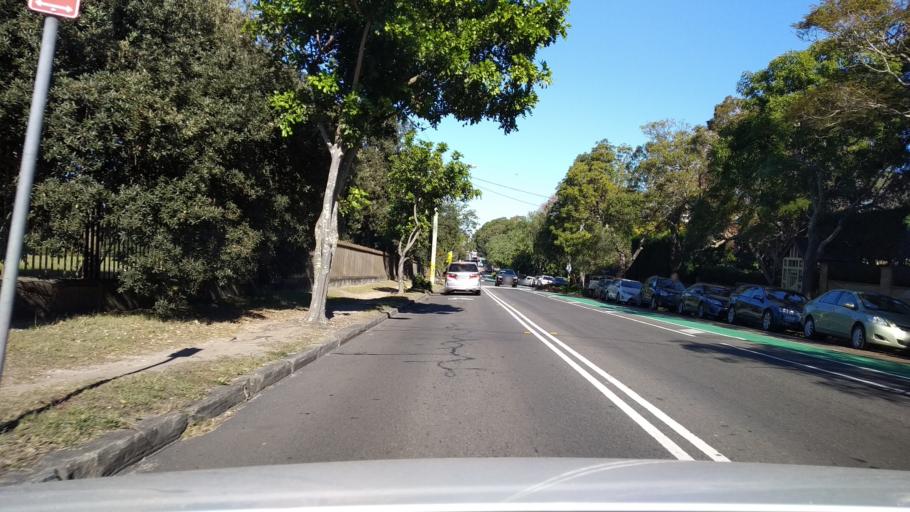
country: AU
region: New South Wales
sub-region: Woollahra
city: Woollahra
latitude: -33.8930
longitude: 151.2318
